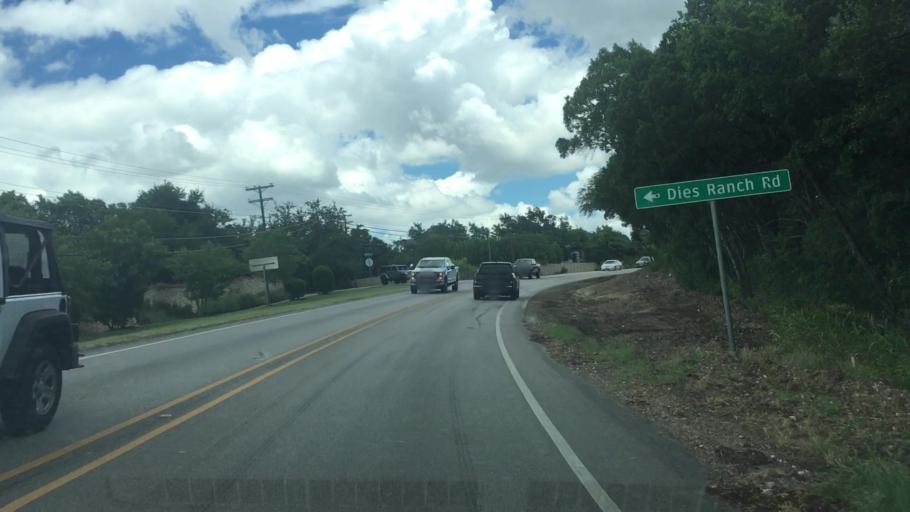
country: US
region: Texas
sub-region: Williamson County
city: Anderson Mill
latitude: 30.4567
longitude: -97.8462
